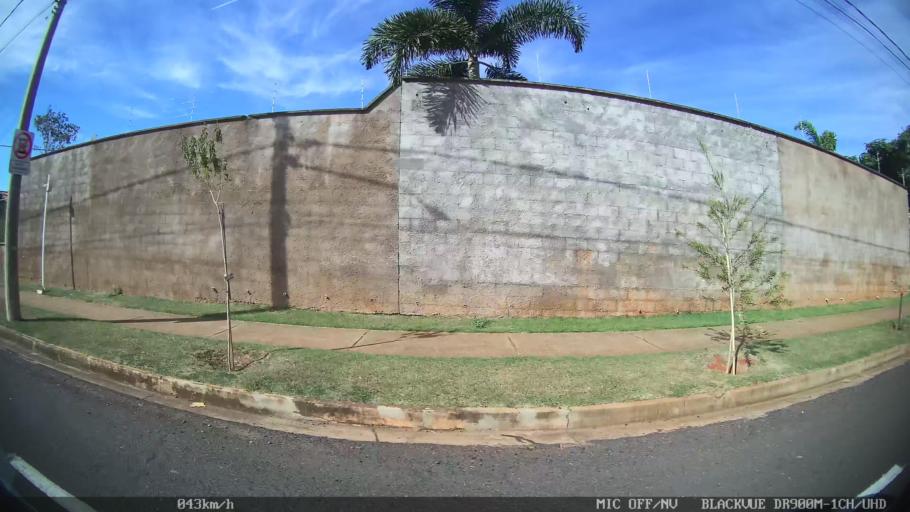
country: BR
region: Sao Paulo
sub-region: Sao Jose Do Rio Preto
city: Sao Jose do Rio Preto
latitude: -20.8035
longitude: -49.3325
